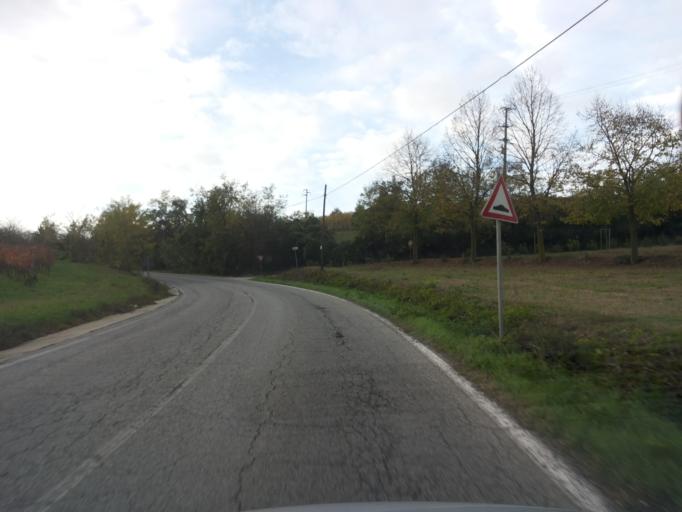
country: IT
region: Piedmont
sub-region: Provincia di Alessandria
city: Ozzano Monferrato
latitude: 45.1090
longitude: 8.3866
